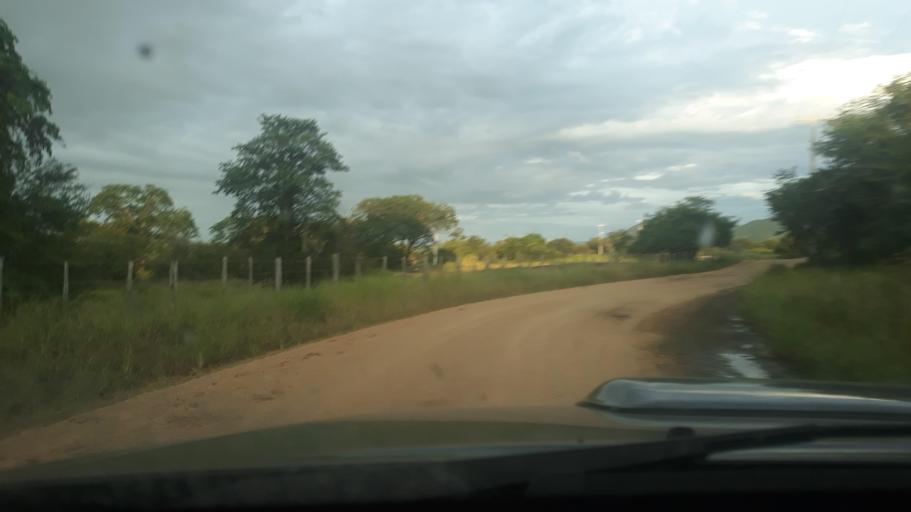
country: BR
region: Bahia
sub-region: Riacho De Santana
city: Riacho de Santana
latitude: -13.9000
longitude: -42.8819
